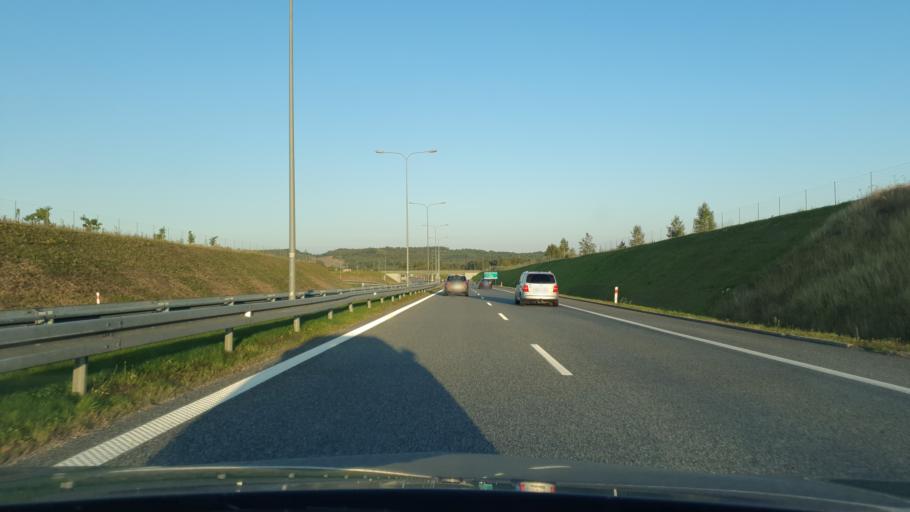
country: PL
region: Pomeranian Voivodeship
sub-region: Powiat slupski
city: Kobylnica
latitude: 54.4250
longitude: 16.9995
